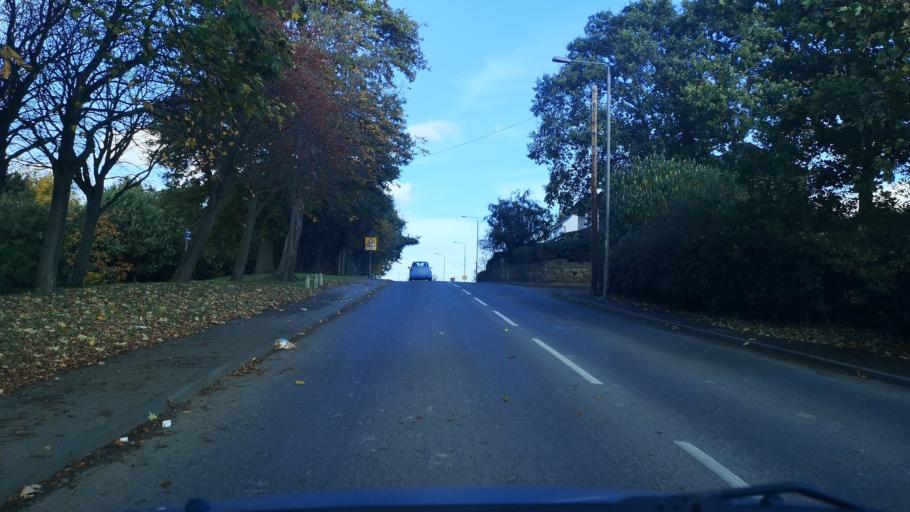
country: GB
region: England
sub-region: City and Borough of Wakefield
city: Featherstone
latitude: 53.6697
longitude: -1.3499
